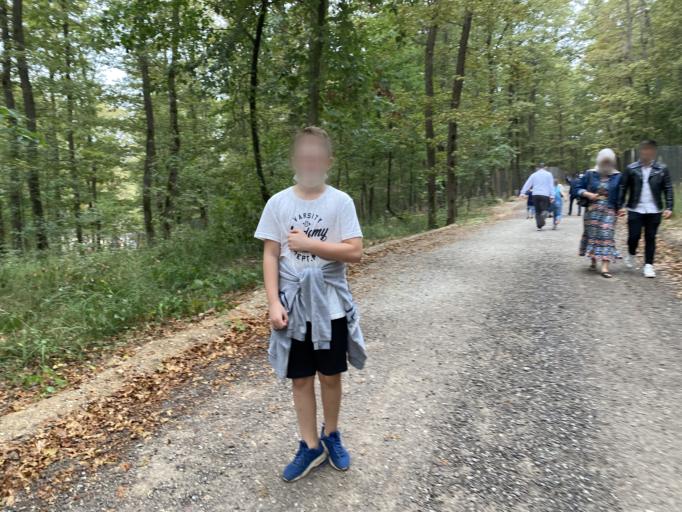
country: TR
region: Kocaeli
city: Derbent
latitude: 40.7375
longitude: 30.1661
